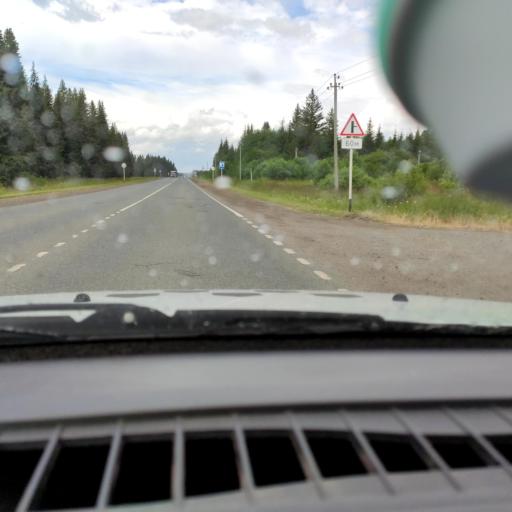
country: RU
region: Perm
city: Orda
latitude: 57.2006
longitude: 56.9187
